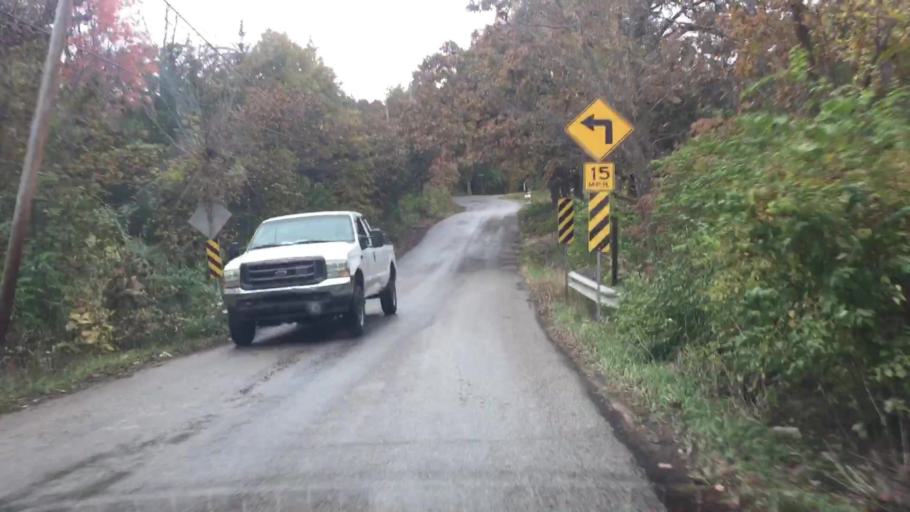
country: US
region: Kansas
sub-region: Wyandotte County
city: Edwardsville
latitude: 38.9926
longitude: -94.8219
